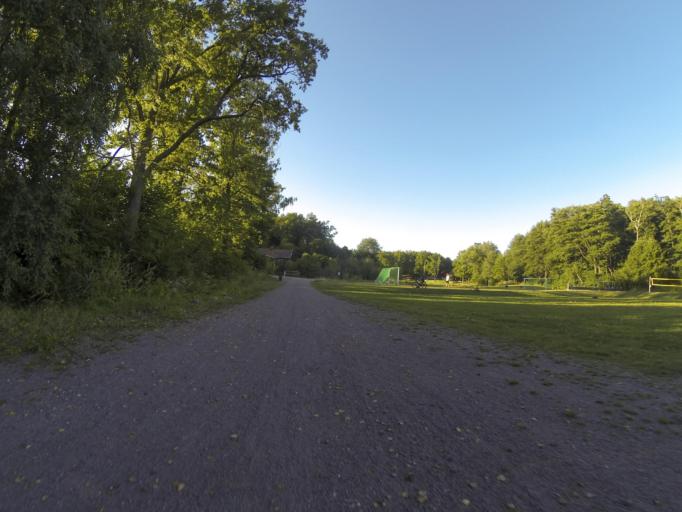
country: SE
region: Vaestmanland
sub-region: Vasteras
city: Vasteras
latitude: 59.5494
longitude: 16.6602
